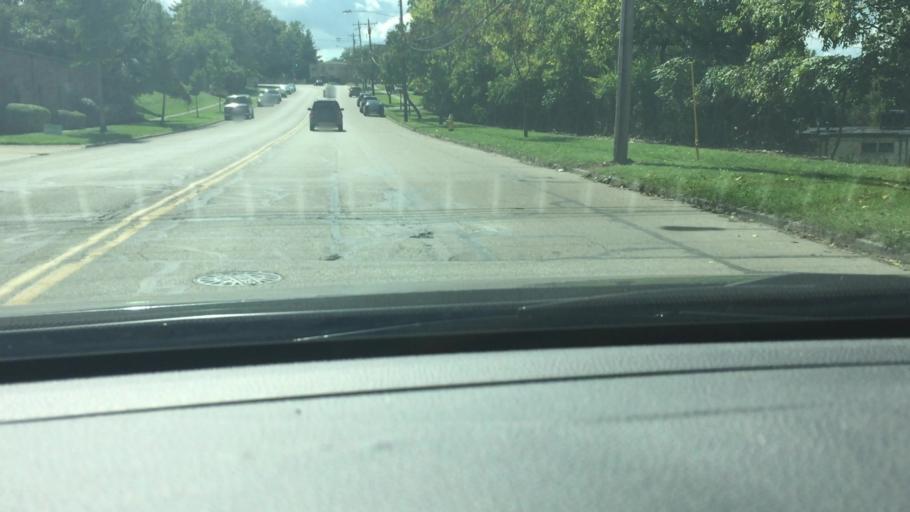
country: US
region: Ohio
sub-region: Hamilton County
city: Fairfax
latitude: 39.1641
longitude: -84.4144
